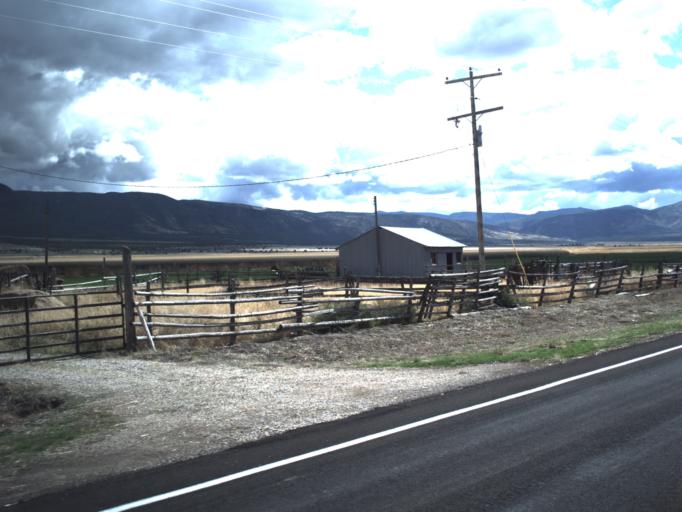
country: US
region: Utah
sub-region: Millard County
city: Fillmore
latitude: 38.8755
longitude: -112.4134
